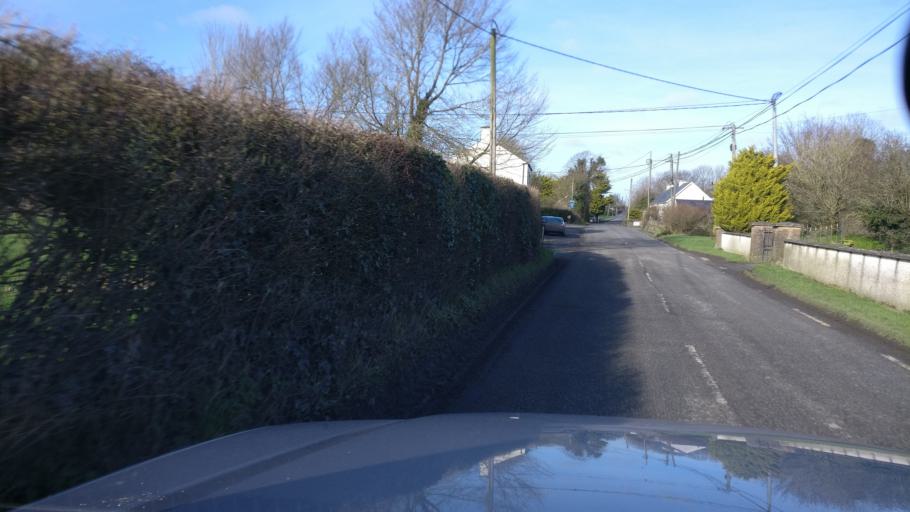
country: IE
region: Leinster
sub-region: Kilkenny
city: Castlecomer
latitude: 52.8651
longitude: -7.1648
